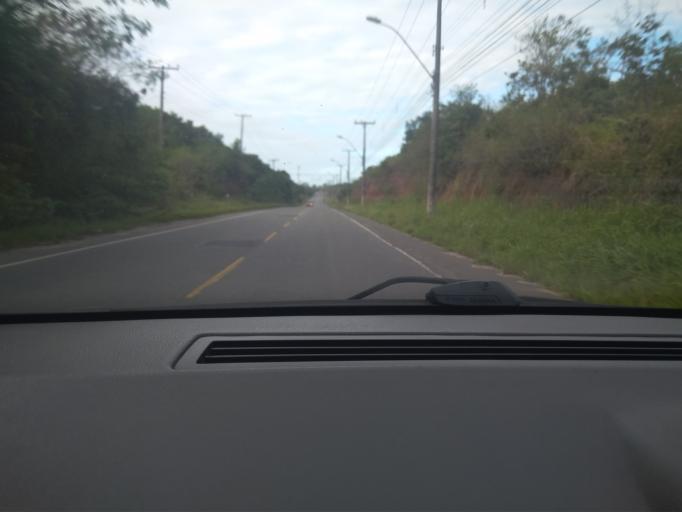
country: BR
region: Espirito Santo
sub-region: Serra
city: Serra
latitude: -20.0949
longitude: -40.1763
